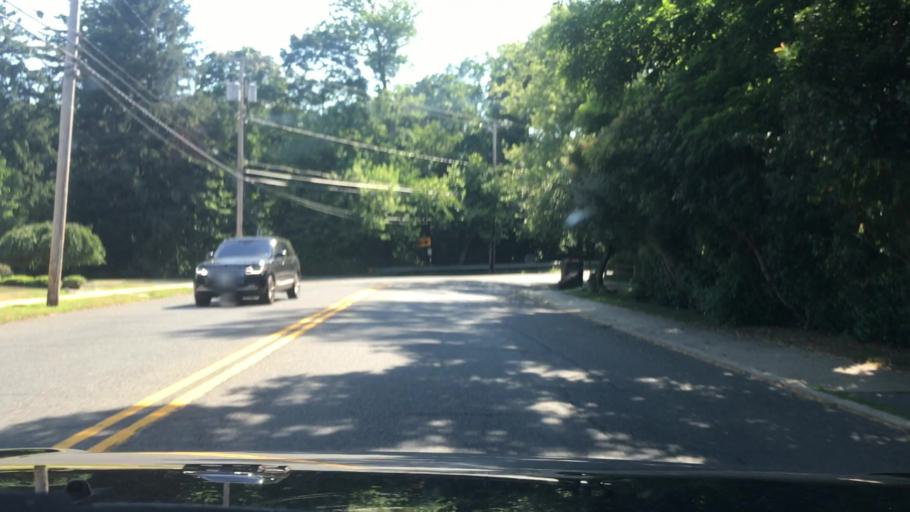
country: US
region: New Jersey
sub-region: Monmouth County
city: Red Bank
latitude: 40.3534
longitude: -74.0589
